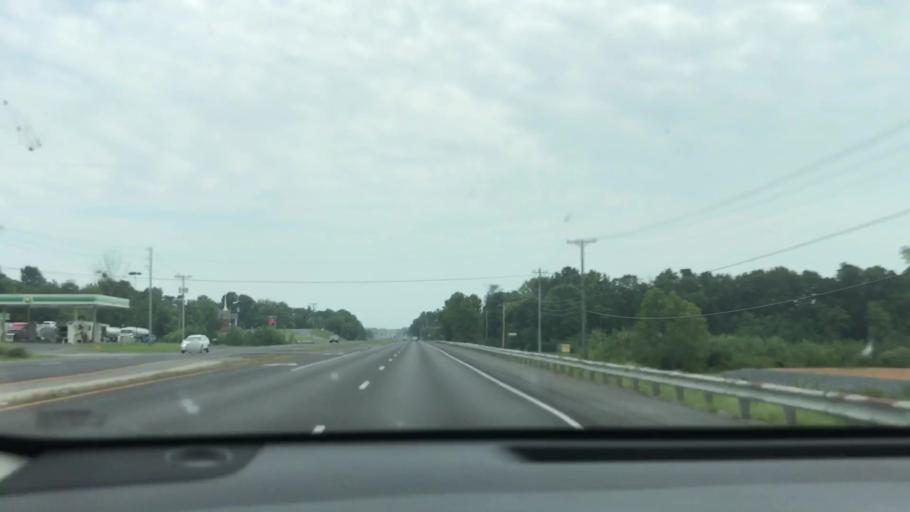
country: US
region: Kentucky
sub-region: Calloway County
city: Murray
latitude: 36.6406
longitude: -88.3090
